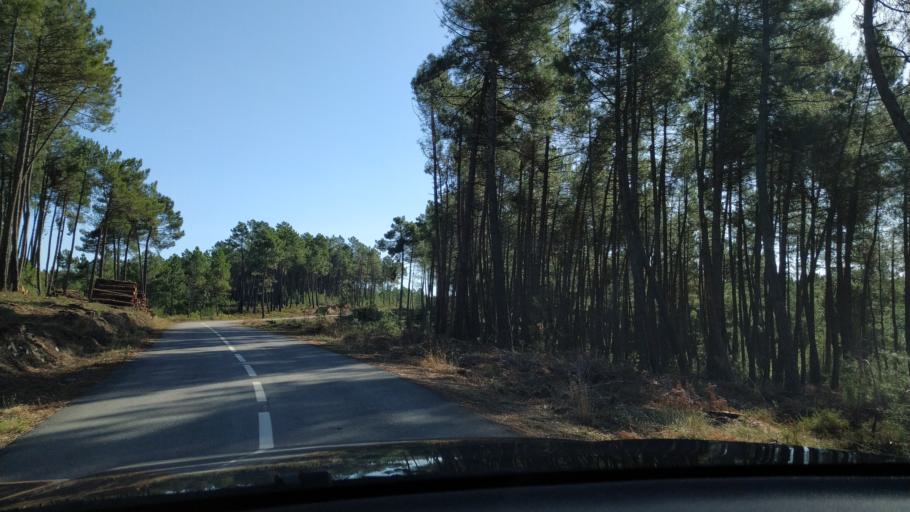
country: PT
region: Vila Real
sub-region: Sabrosa
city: Vilela
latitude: 41.2295
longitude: -7.6205
